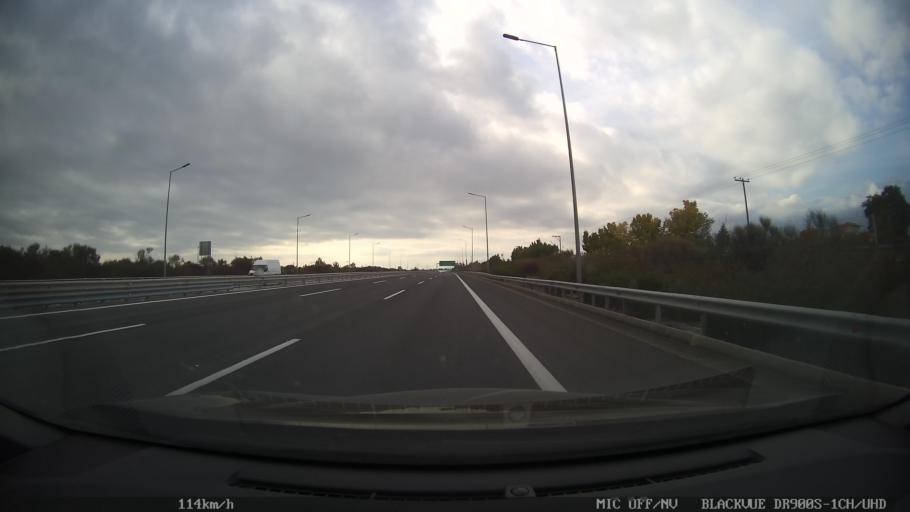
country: GR
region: Central Macedonia
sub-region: Nomos Pierias
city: Litochoro
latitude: 40.1403
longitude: 22.5433
